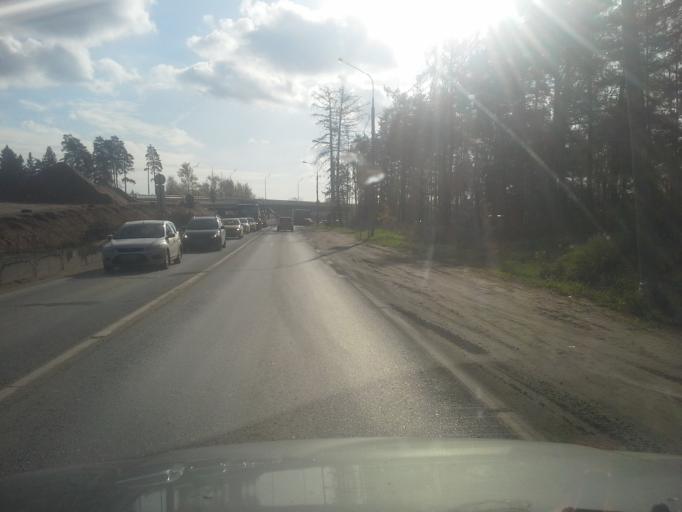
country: RU
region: Moskovskaya
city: Zvenigorod
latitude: 55.7031
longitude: 36.8799
